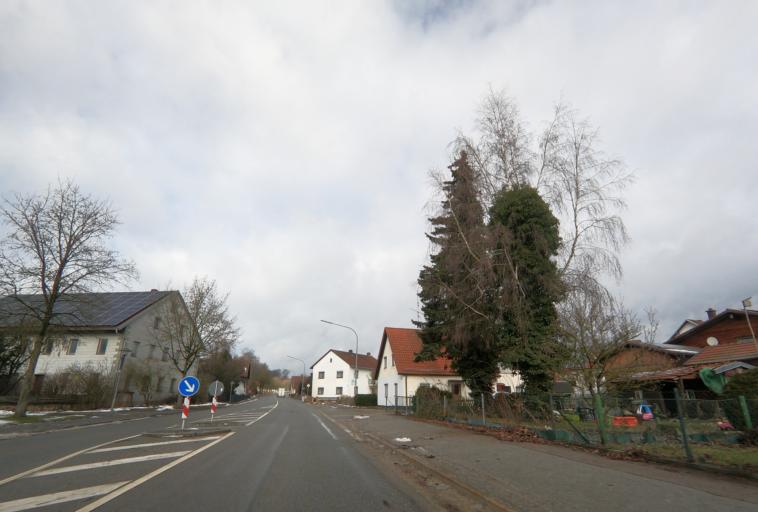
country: DE
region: Bavaria
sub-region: Lower Bavaria
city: Mallersdorf-Pfaffenberg
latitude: 48.7840
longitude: 12.1816
